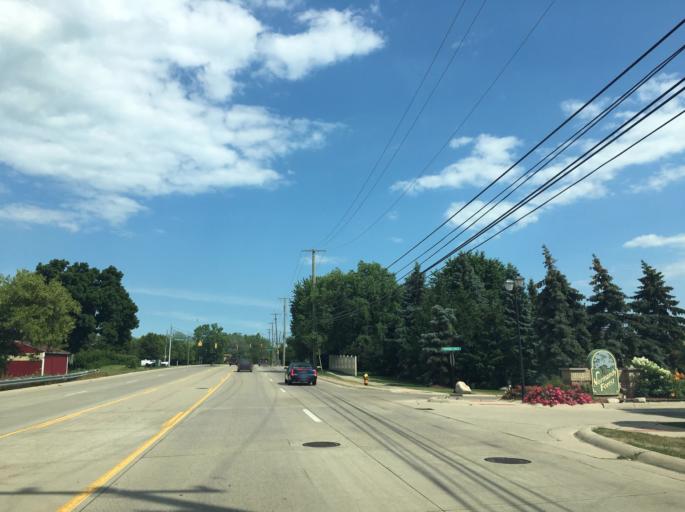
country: US
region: Michigan
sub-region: Macomb County
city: Clinton
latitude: 42.6061
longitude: -82.9195
